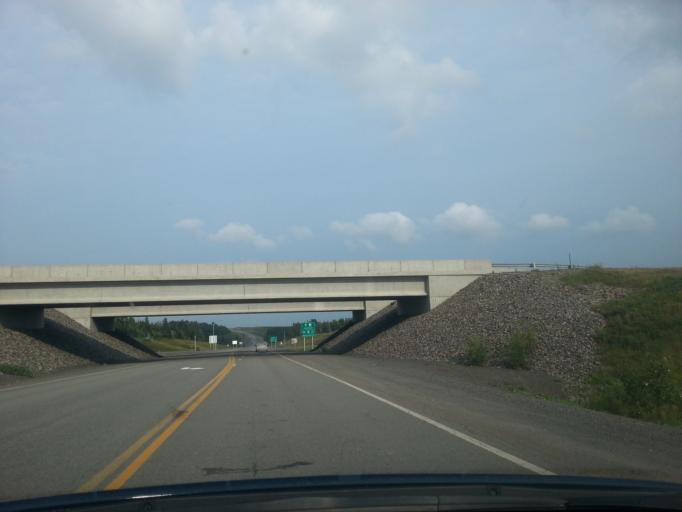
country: CA
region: New Brunswick
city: Florenceville-Bristol
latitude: 46.2865
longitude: -67.5786
